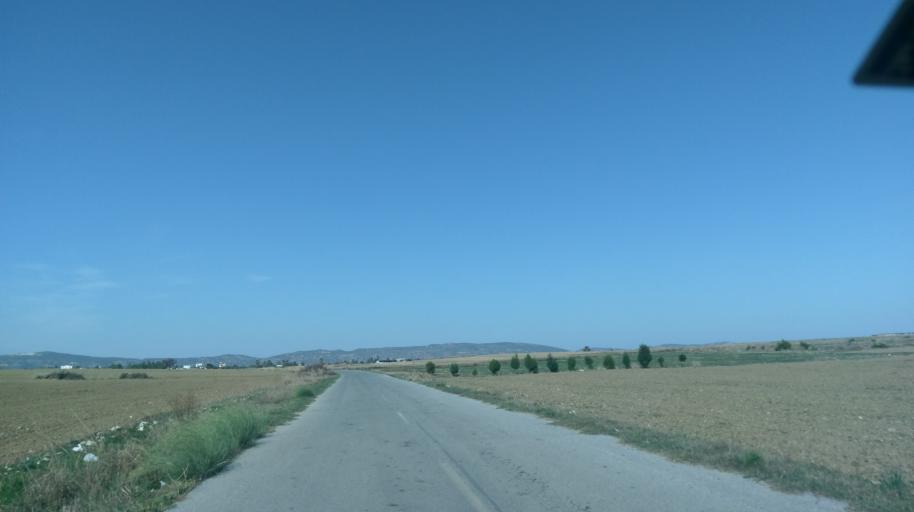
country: CY
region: Ammochostos
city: Leonarisso
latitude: 35.3814
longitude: 34.0209
